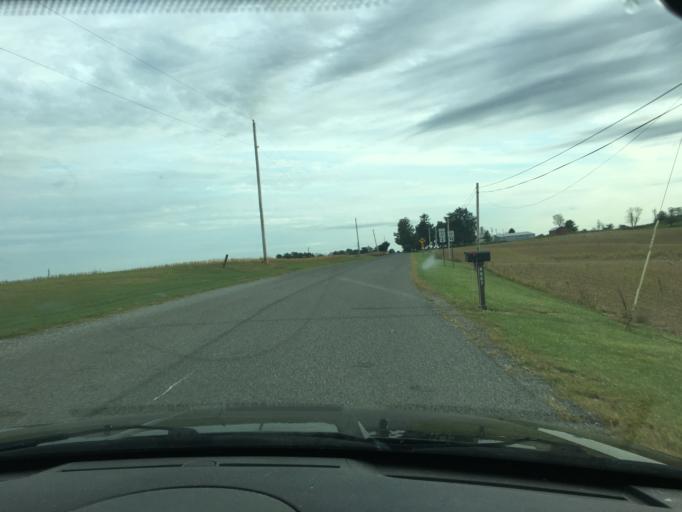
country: US
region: Ohio
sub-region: Logan County
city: West Liberty
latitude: 40.2989
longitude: -83.6848
